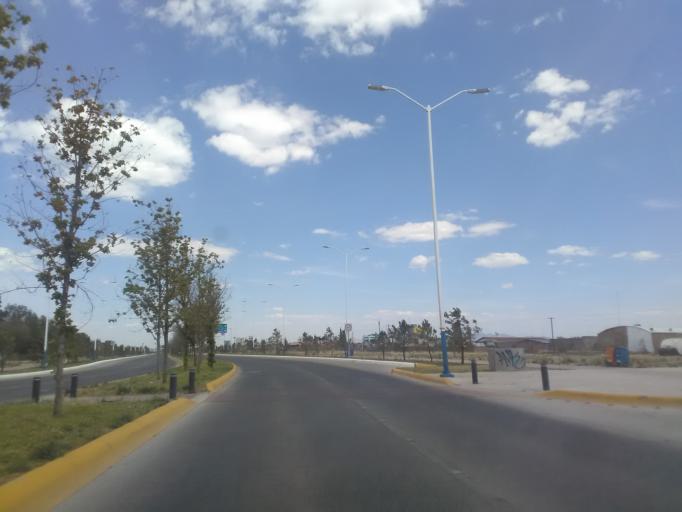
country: MX
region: Durango
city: Victoria de Durango
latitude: 24.0365
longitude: -104.6699
